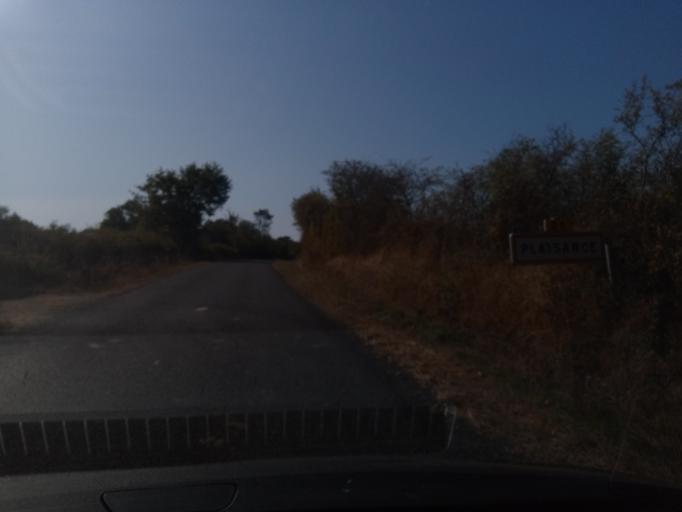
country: FR
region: Poitou-Charentes
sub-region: Departement de la Vienne
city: Saulge
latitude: 46.3374
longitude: 0.8744
